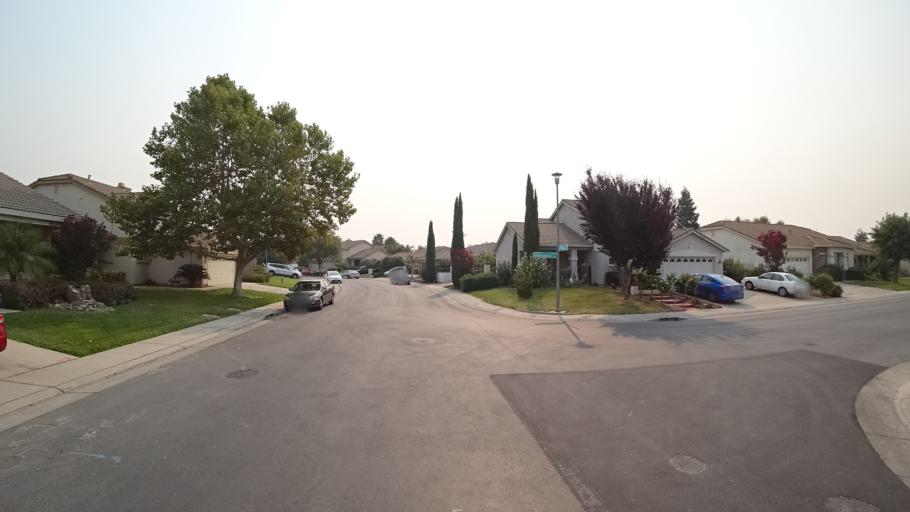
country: US
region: California
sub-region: Sacramento County
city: Laguna
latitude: 38.3958
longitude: -121.4351
